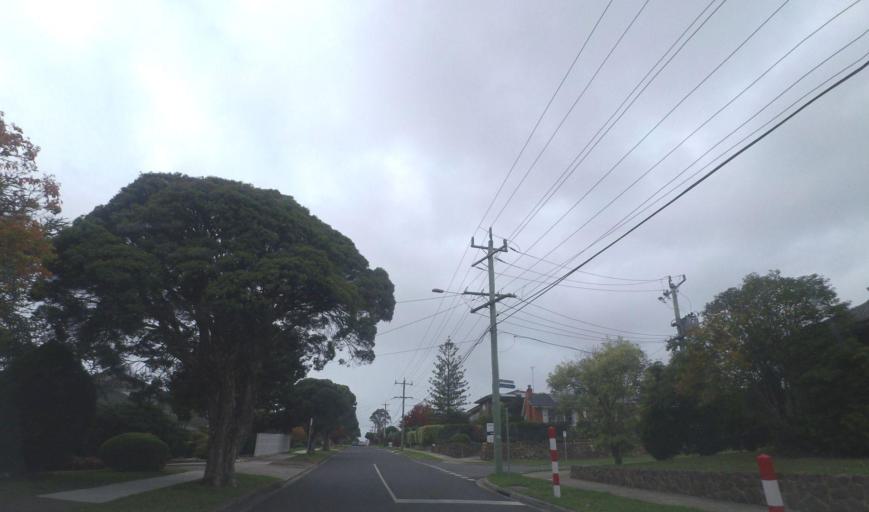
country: AU
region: Victoria
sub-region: Whitehorse
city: Mont Albert North
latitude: -37.7915
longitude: 145.1131
